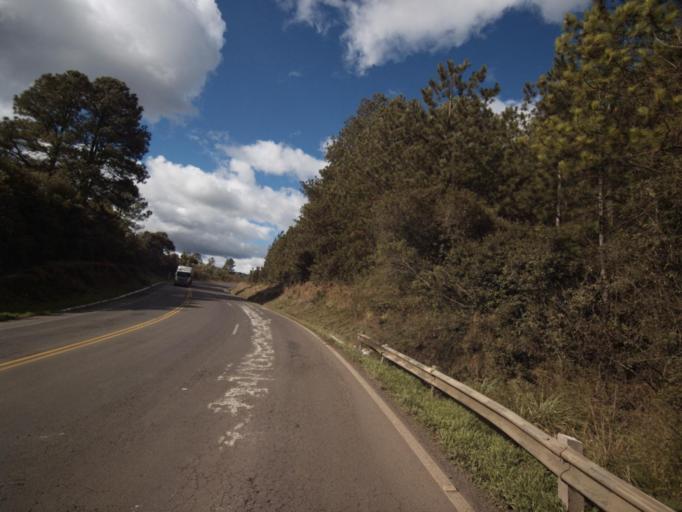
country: BR
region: Santa Catarina
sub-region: Joacaba
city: Joacaba
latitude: -27.0601
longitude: -51.6786
